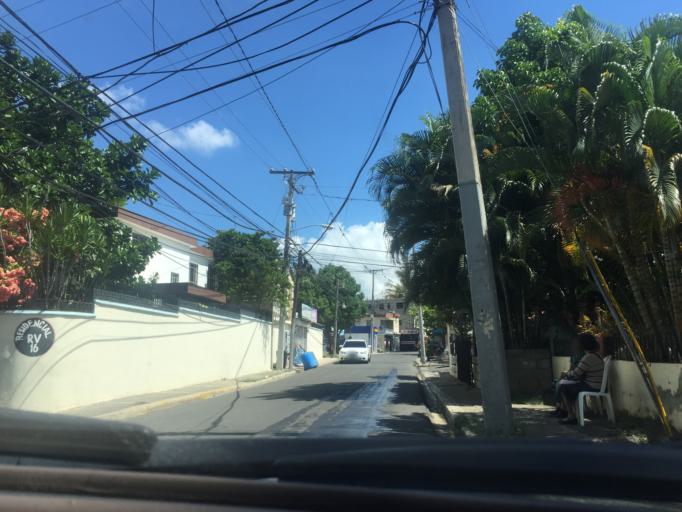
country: DO
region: Santiago
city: Santiago de los Caballeros
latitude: 19.4625
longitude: -70.6605
